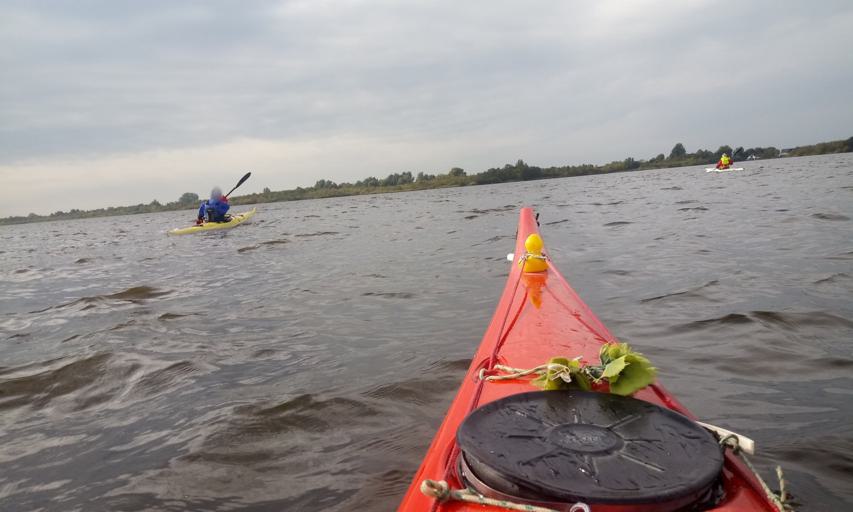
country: NL
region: North Holland
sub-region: Gemeente Wijdemeren
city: Oud-Loosdrecht
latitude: 52.1853
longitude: 5.0821
